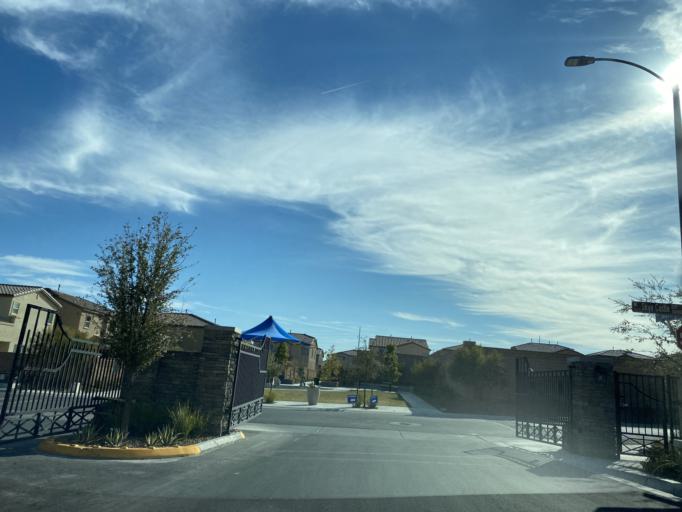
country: US
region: Nevada
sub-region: Clark County
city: Summerlin South
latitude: 36.3102
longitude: -115.3171
